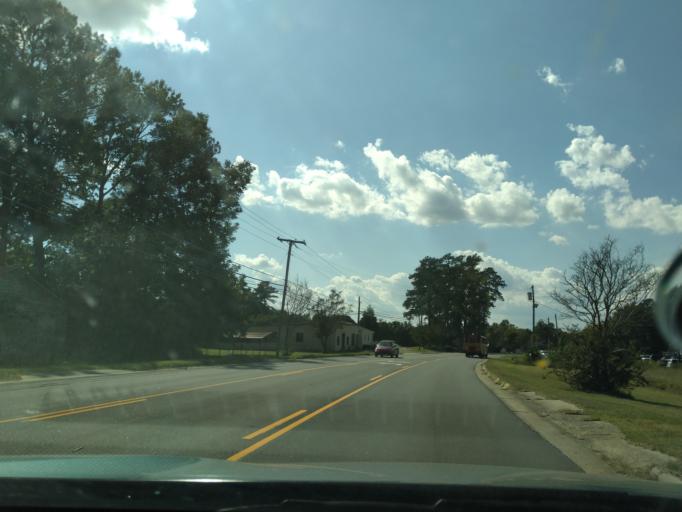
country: US
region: North Carolina
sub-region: Martin County
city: Robersonville
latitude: 35.8241
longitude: -77.2647
